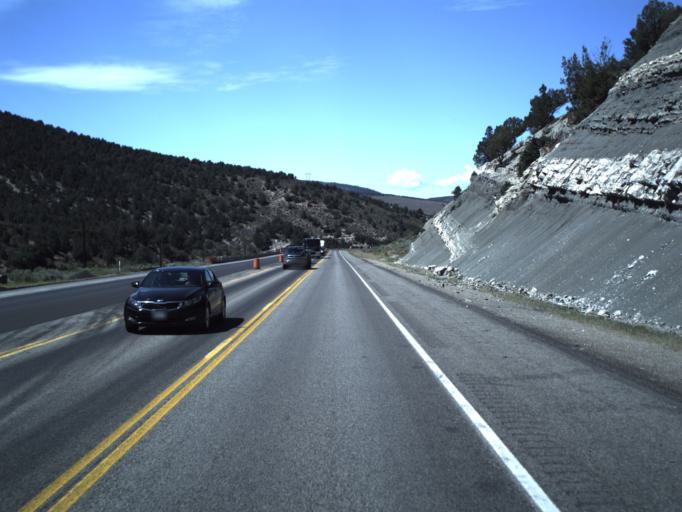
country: US
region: Utah
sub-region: Utah County
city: Mapleton
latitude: 39.9551
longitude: -111.2553
